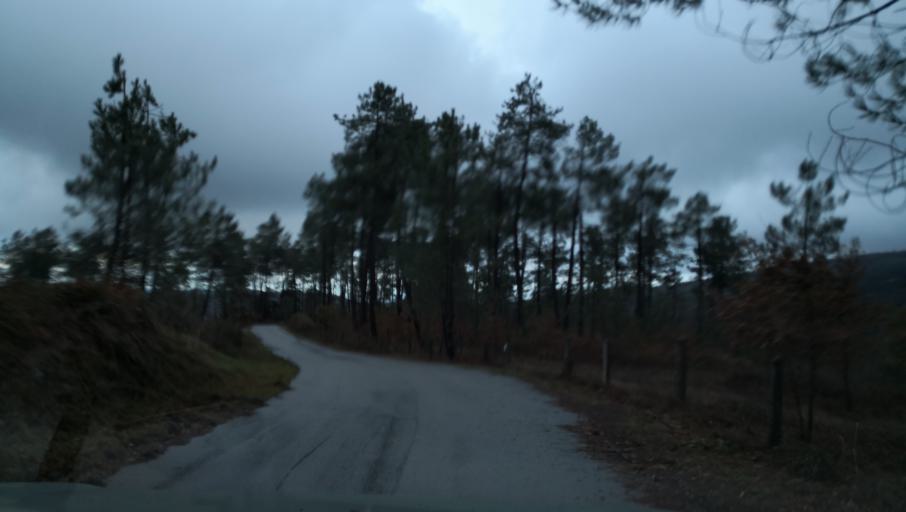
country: PT
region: Vila Real
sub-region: Santa Marta de Penaguiao
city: Santa Marta de Penaguiao
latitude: 41.2942
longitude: -7.8884
